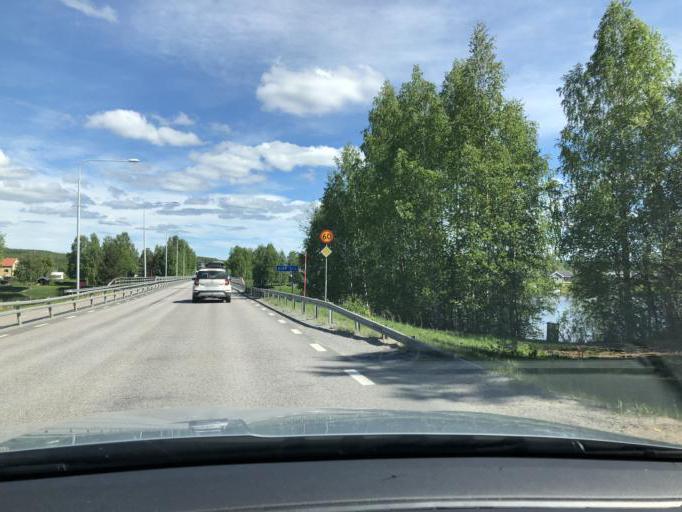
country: SE
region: Norrbotten
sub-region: Alvsbyns Kommun
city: AElvsbyn
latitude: 65.6660
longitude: 21.0336
